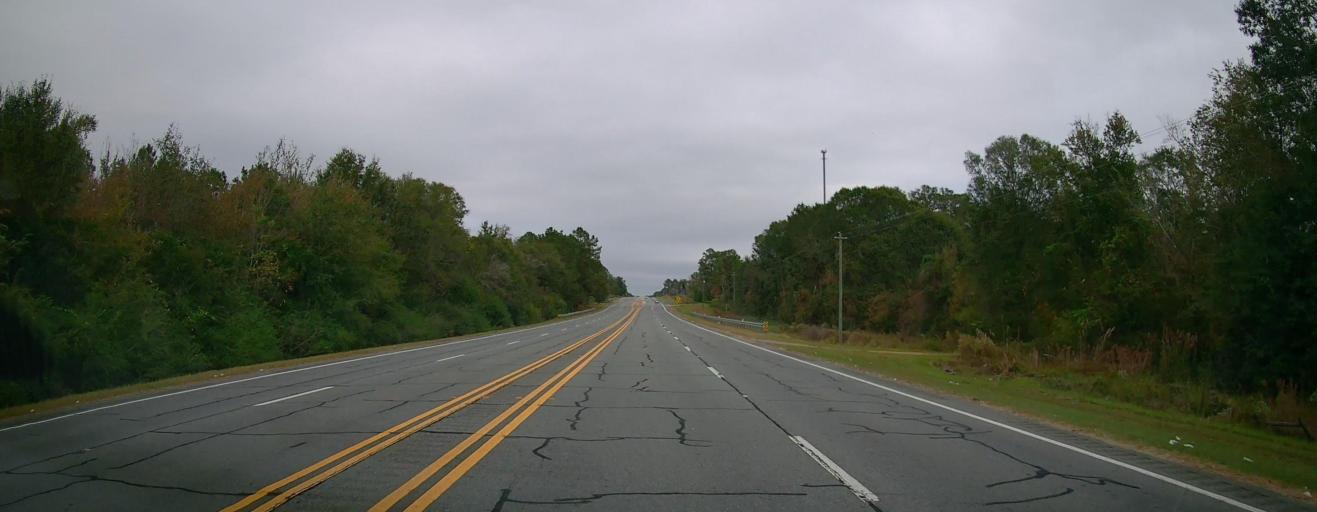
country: US
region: Georgia
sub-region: Tift County
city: Omega
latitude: 31.3128
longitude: -83.6323
